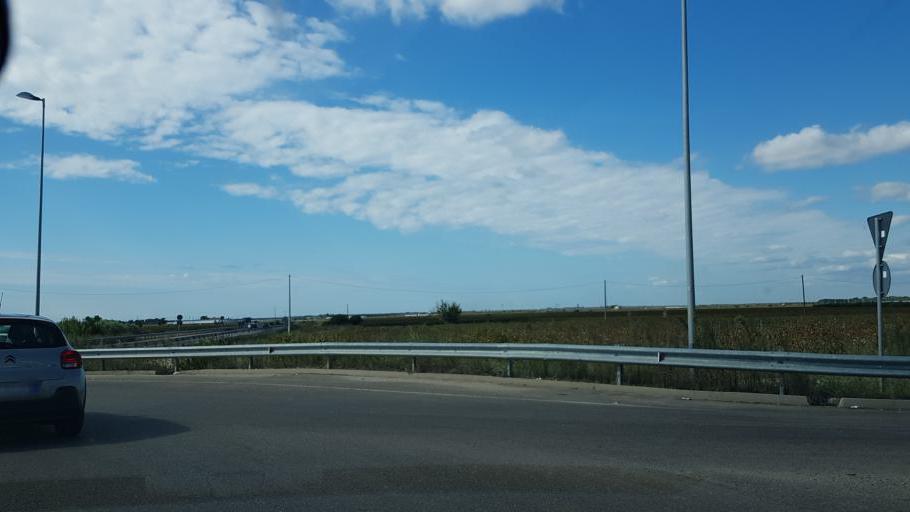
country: IT
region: Apulia
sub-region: Provincia di Lecce
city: Leverano
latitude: 40.3059
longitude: 17.9897
